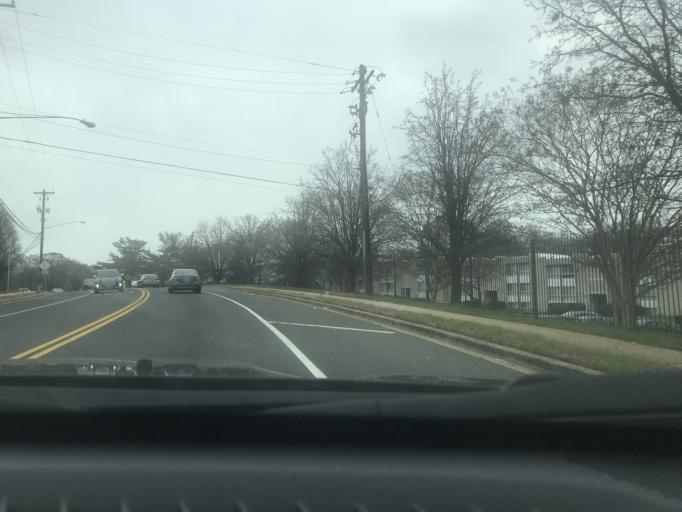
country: US
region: Maryland
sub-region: Prince George's County
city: Temple Hills
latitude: 38.8039
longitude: -76.9556
